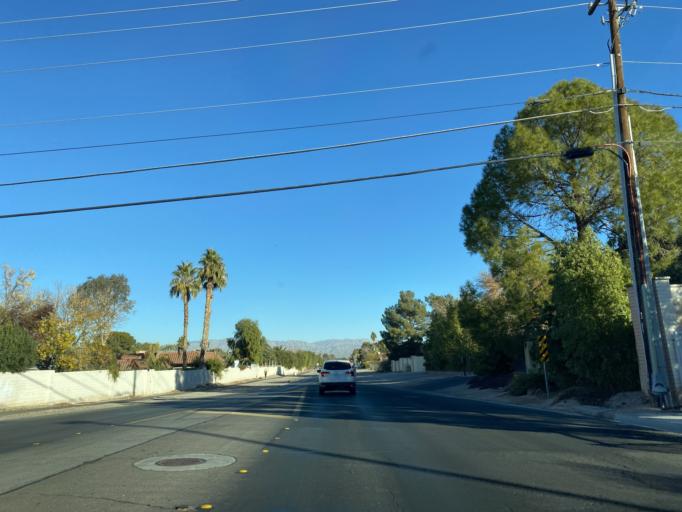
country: US
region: Nevada
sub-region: Clark County
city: Winchester
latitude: 36.1166
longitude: -115.1098
